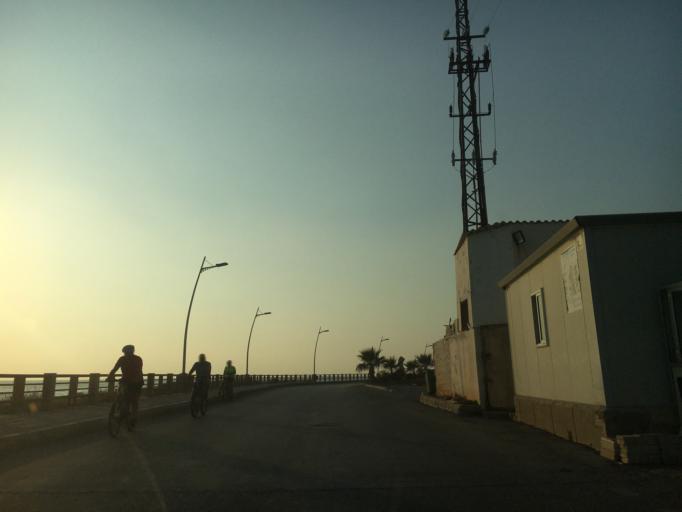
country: LB
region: Mont-Liban
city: Jbail
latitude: 34.1420
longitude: 35.6291
